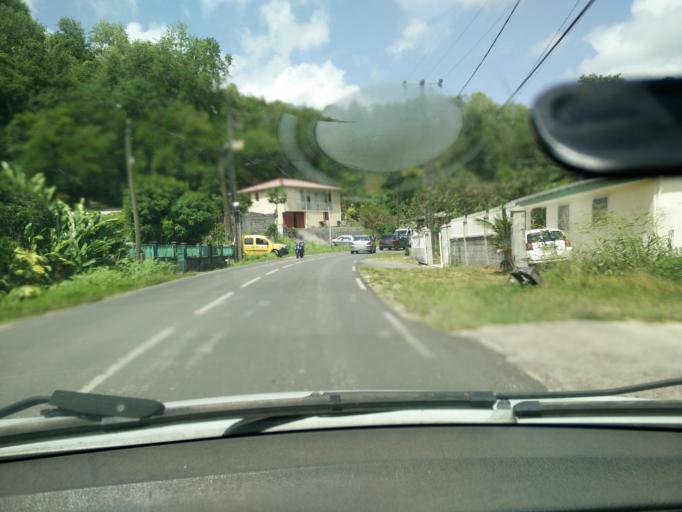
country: GP
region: Guadeloupe
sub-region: Guadeloupe
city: Les Abymes
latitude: 16.2890
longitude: -61.4676
